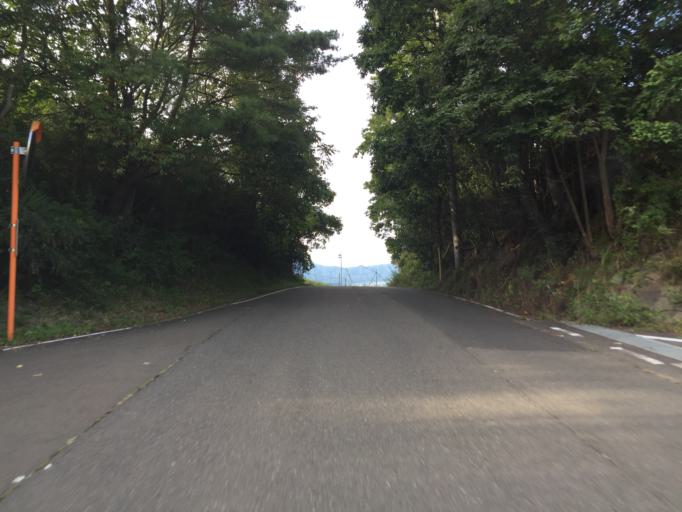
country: JP
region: Fukushima
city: Hobaramachi
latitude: 37.8007
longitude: 140.5277
